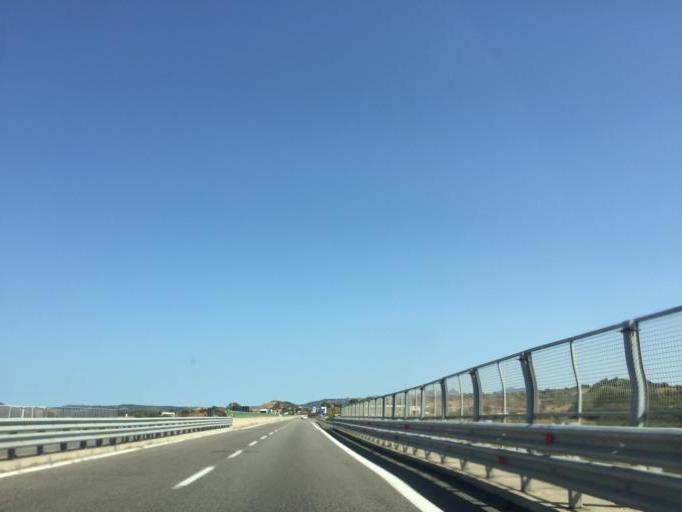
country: IT
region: Sardinia
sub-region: Provincia di Olbia-Tempio
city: Olbia
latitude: 40.8895
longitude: 9.4906
